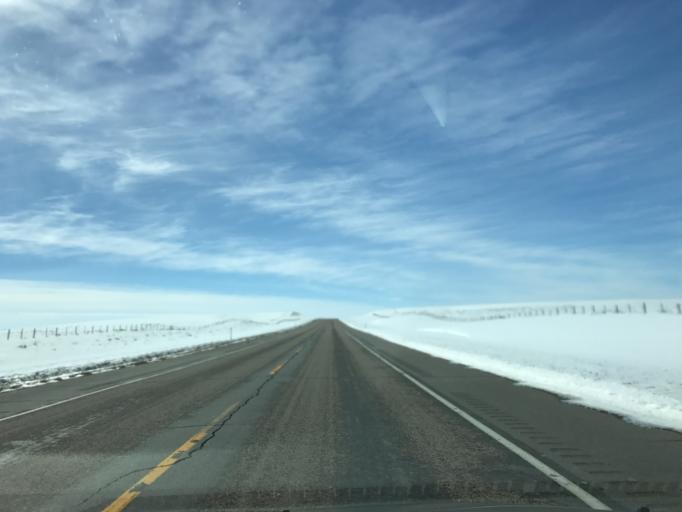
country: US
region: Wyoming
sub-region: Sublette County
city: Pinedale
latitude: 42.7734
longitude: -110.0529
